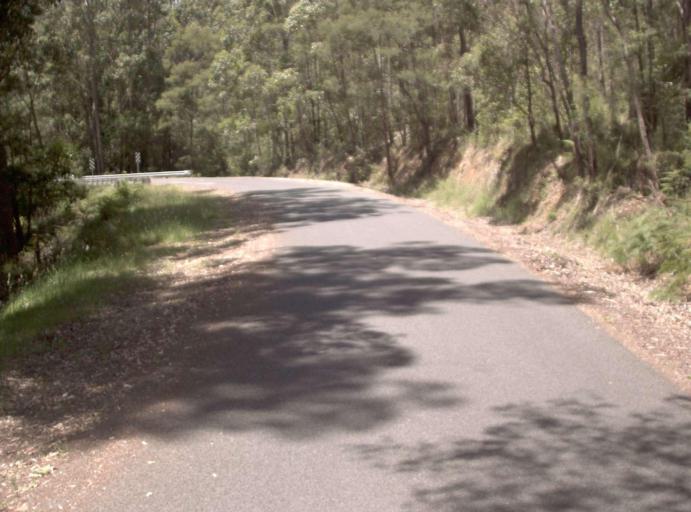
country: AU
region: New South Wales
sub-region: Bombala
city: Bombala
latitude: -37.5351
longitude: 148.9284
